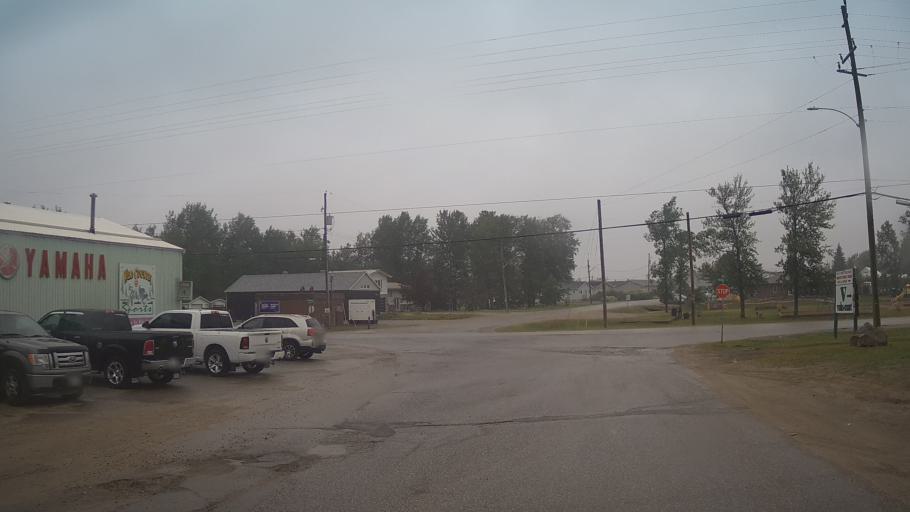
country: CA
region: Ontario
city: Greenstone
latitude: 49.7745
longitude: -86.5377
